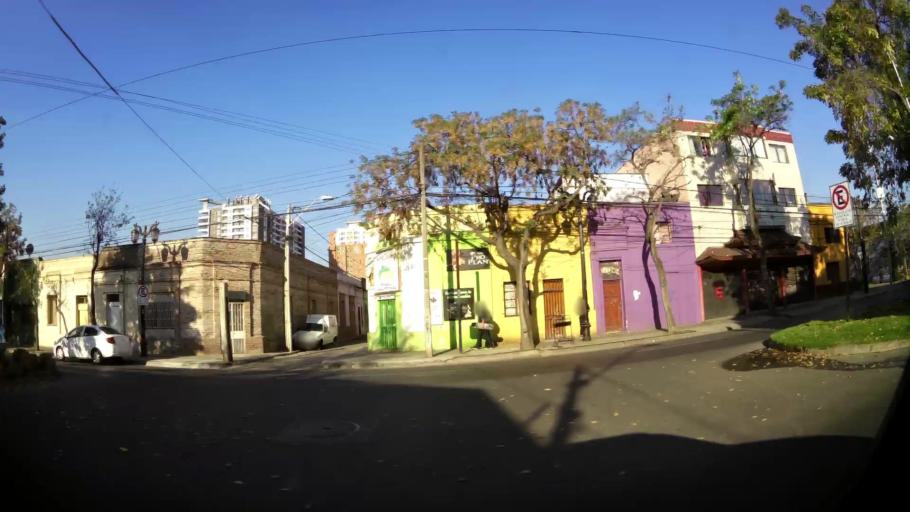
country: CL
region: Santiago Metropolitan
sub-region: Provincia de Santiago
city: Santiago
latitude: -33.4307
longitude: -70.6694
